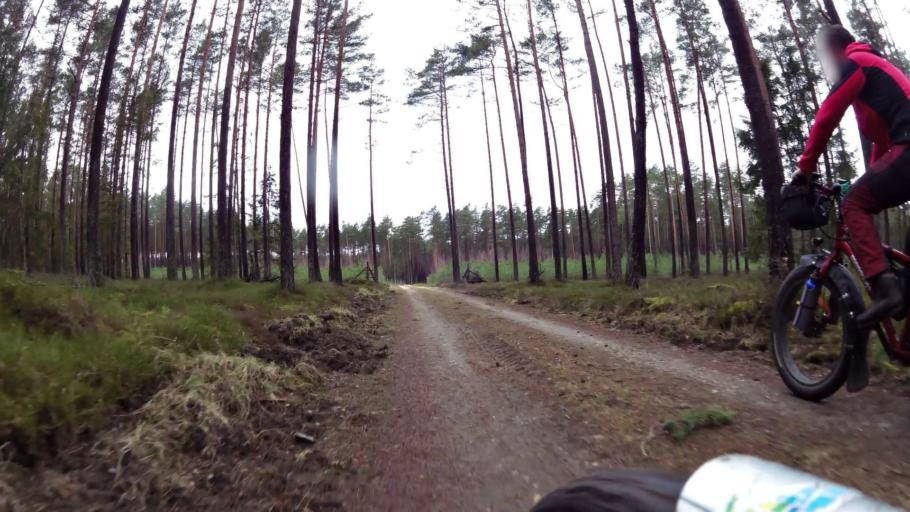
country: PL
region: Pomeranian Voivodeship
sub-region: Powiat bytowski
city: Borzytuchom
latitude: 54.2649
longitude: 17.3967
